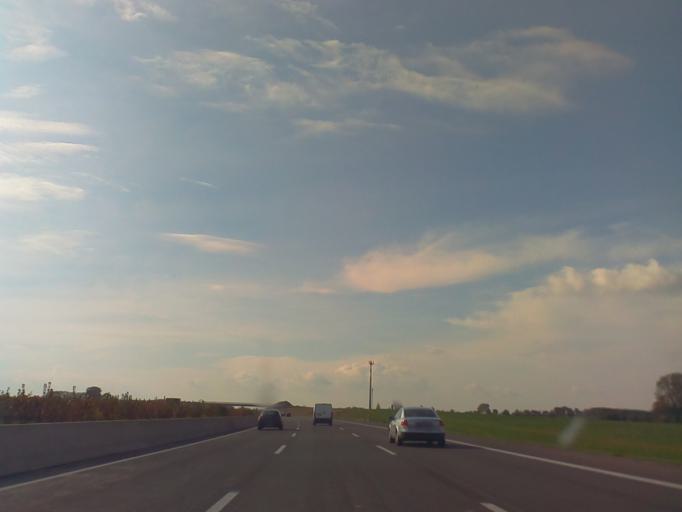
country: DE
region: Thuringia
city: Bischofroda
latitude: 51.0172
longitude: 10.3579
